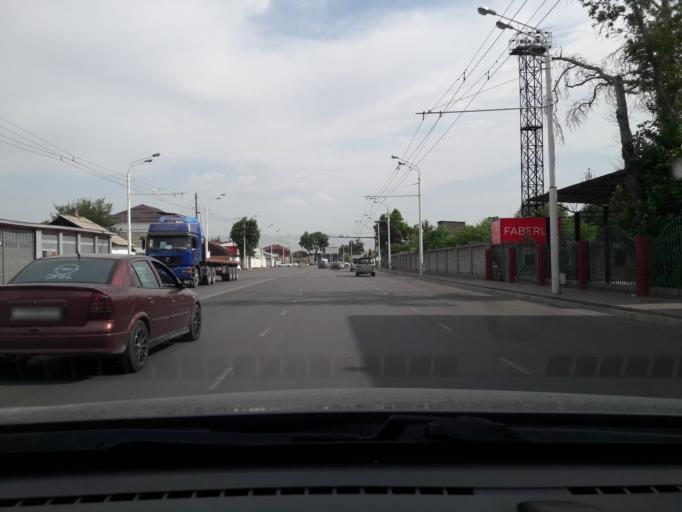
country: TJ
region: Dushanbe
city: Dushanbe
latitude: 38.5422
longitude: 68.7553
